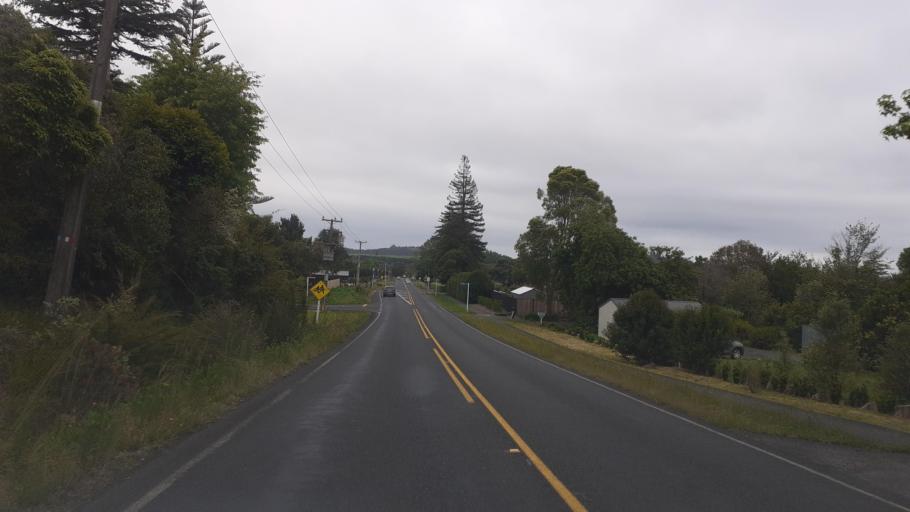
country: NZ
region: Northland
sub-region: Far North District
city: Kerikeri
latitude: -35.2104
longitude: 173.9627
